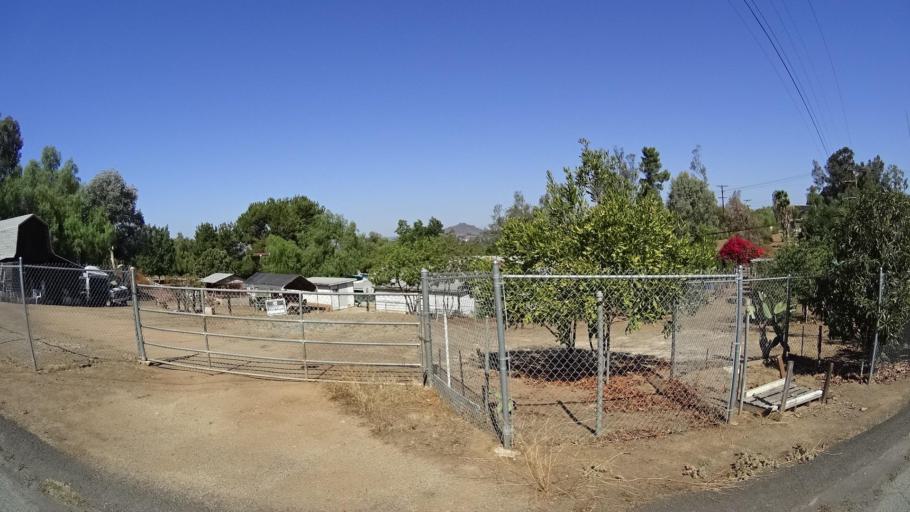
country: US
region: California
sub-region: San Diego County
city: Granite Hills
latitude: 32.7905
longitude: -116.9067
